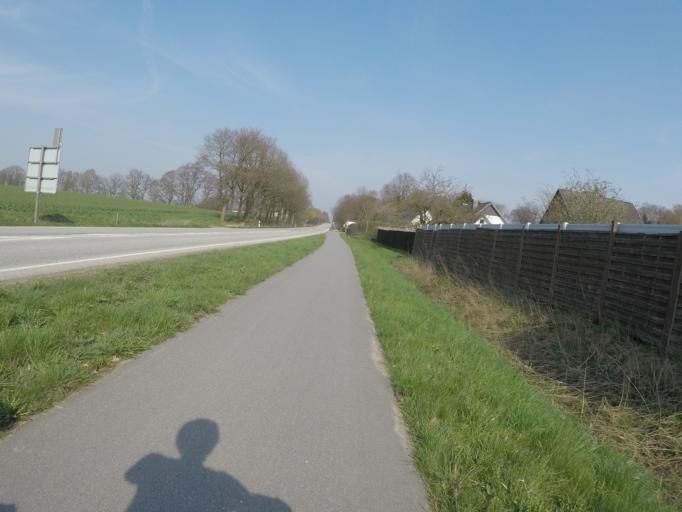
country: DE
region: Schleswig-Holstein
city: Seth
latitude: 53.8252
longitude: 10.1960
